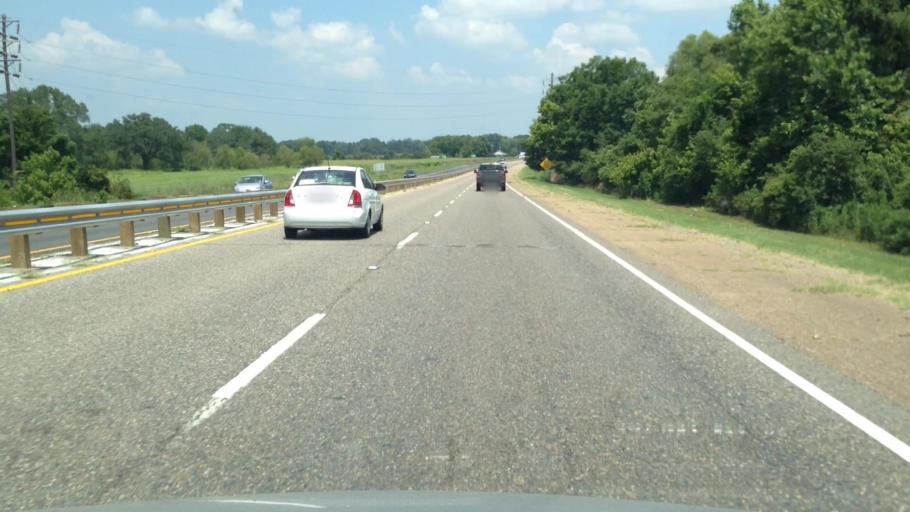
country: US
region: Louisiana
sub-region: Saint Landry Parish
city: Krotz Springs
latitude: 30.5568
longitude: -91.6570
